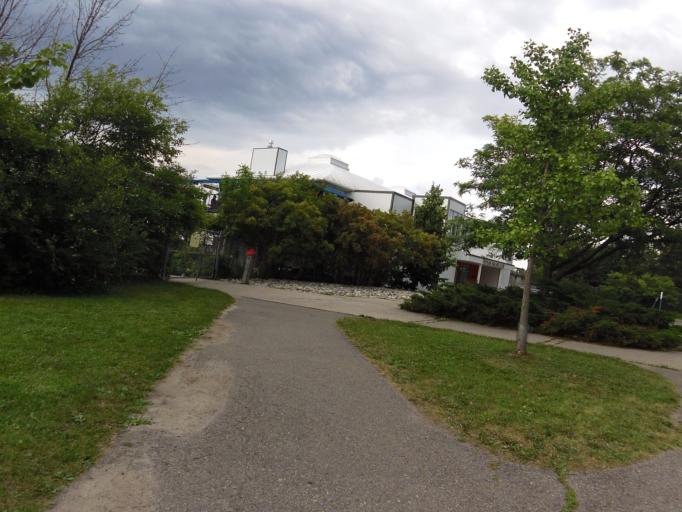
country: CA
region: Ontario
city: Bells Corners
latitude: 45.3512
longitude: -75.8271
